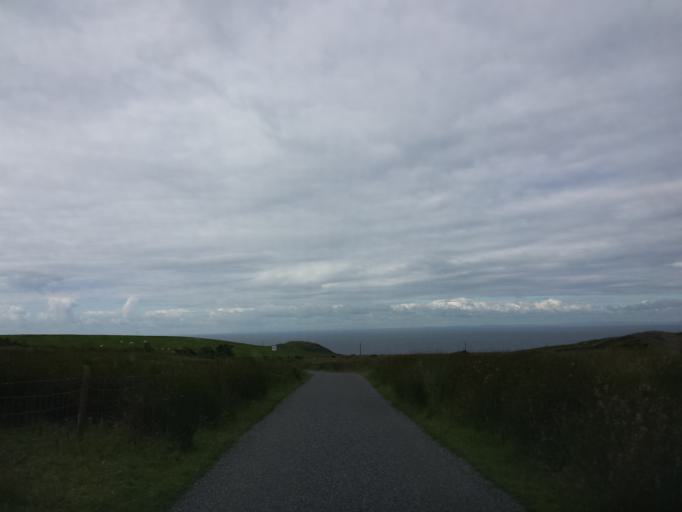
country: GB
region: Scotland
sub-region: Dumfries and Galloway
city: Stranraer
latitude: 54.8689
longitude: -5.1273
